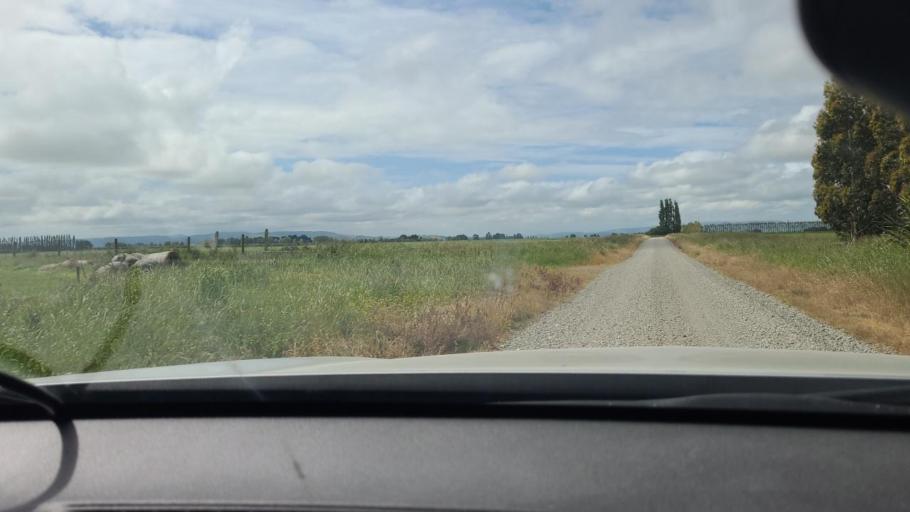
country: NZ
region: Southland
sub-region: Southland District
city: Winton
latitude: -46.1153
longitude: 168.2566
